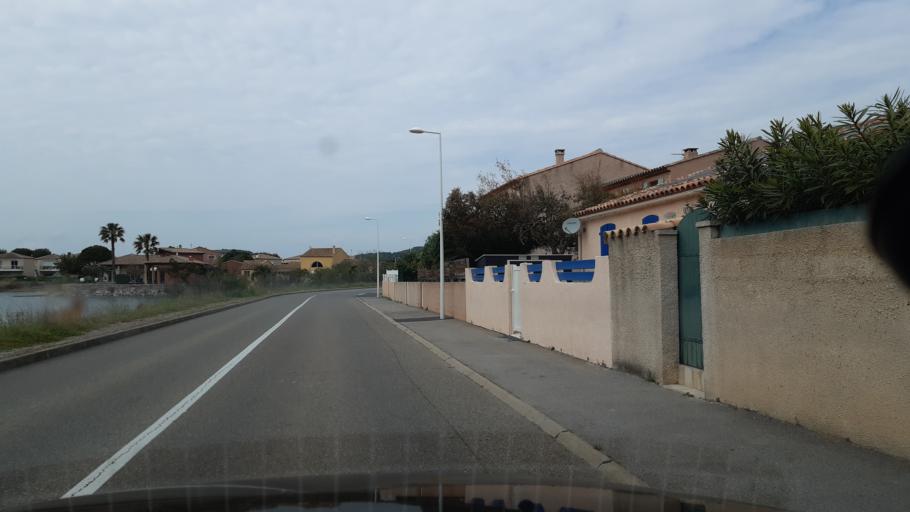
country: FR
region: Languedoc-Roussillon
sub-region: Departement de l'Aude
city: Gruissan
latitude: 43.1144
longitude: 3.0979
